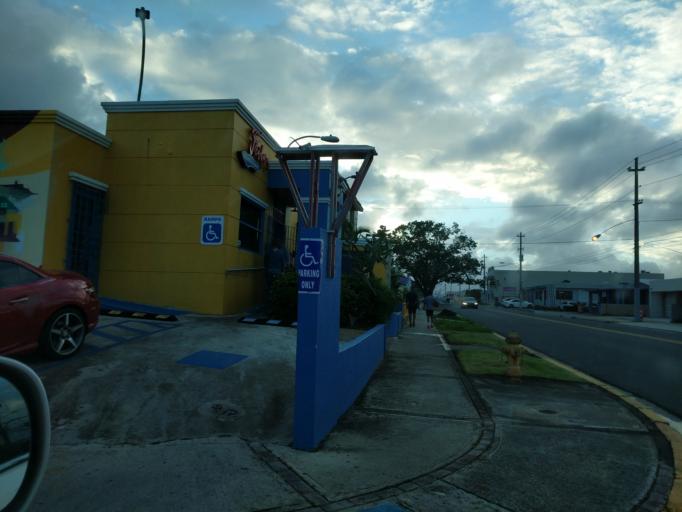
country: PR
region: Catano
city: Catano
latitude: 18.4154
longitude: -66.0587
